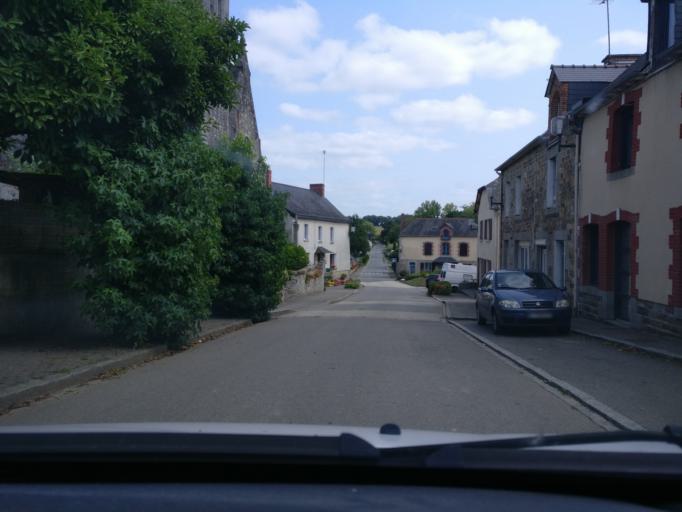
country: FR
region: Brittany
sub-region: Departement d'Ille-et-Vilaine
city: Chevaigne
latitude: 48.2319
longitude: -1.6091
